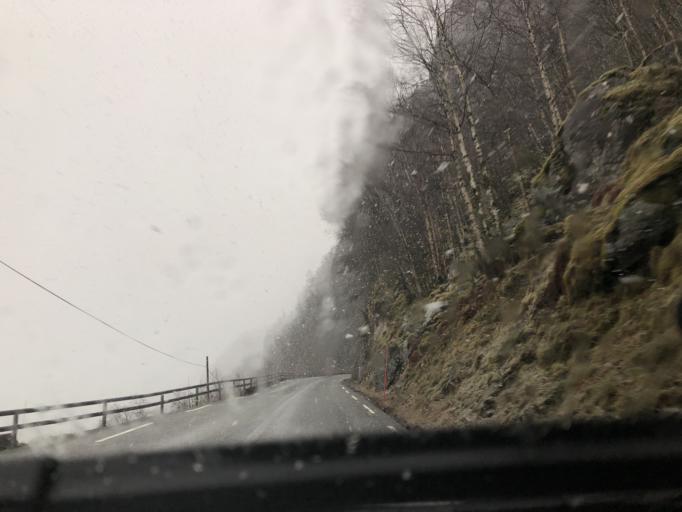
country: NO
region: Rogaland
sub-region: Suldal
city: Sand
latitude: 59.4114
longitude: 6.2152
